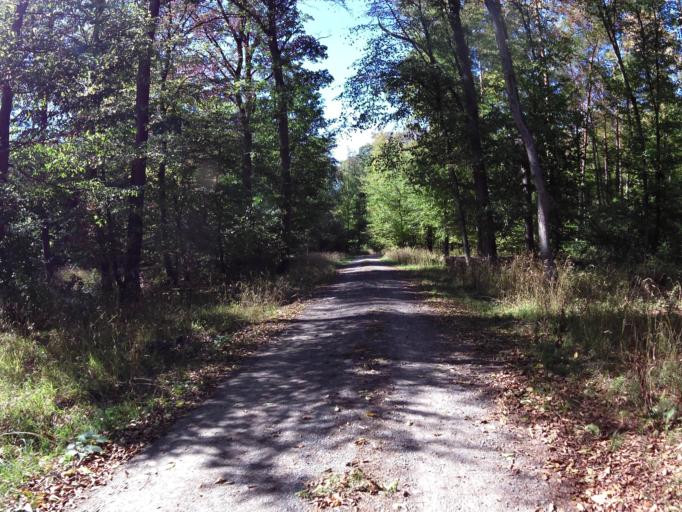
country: DE
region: Bavaria
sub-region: Regierungsbezirk Unterfranken
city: Waldbrunn
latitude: 49.7766
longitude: 9.8156
